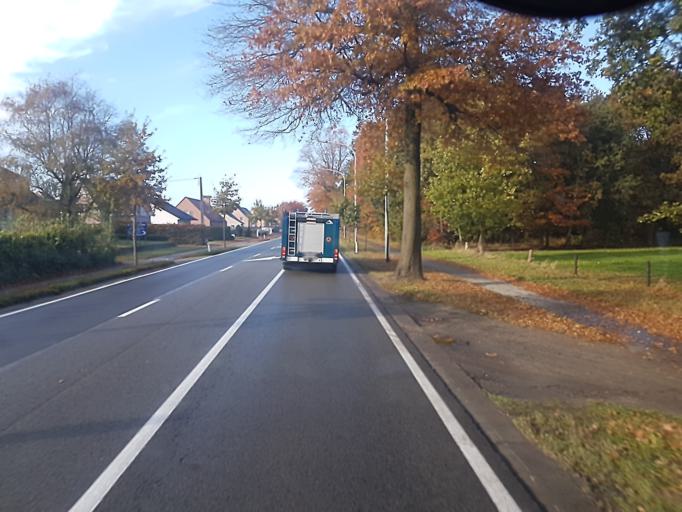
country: BE
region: Flanders
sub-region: Provincie Antwerpen
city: Rijkevorsel
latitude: 51.3019
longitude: 4.7925
